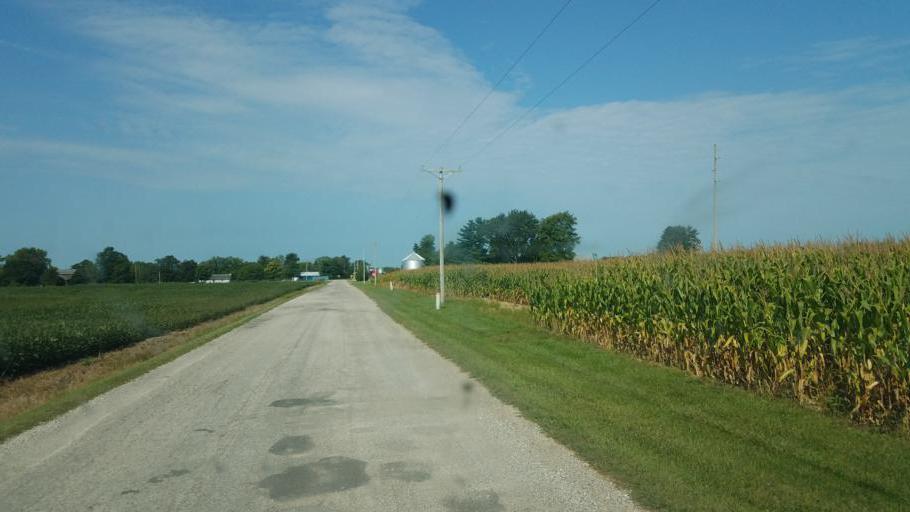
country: US
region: Ohio
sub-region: Morrow County
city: Cardington
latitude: 40.4843
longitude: -82.9511
